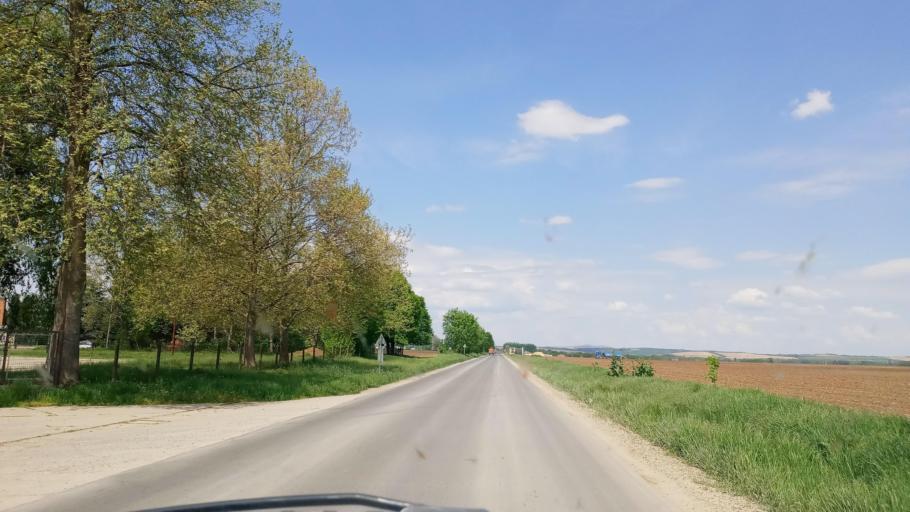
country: HU
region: Baranya
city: Boly
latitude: 45.9424
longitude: 18.5411
